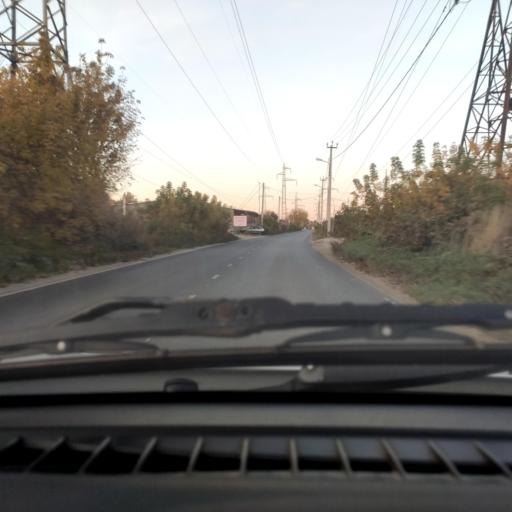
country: RU
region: Samara
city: Zhigulevsk
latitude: 53.5203
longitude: 49.4856
